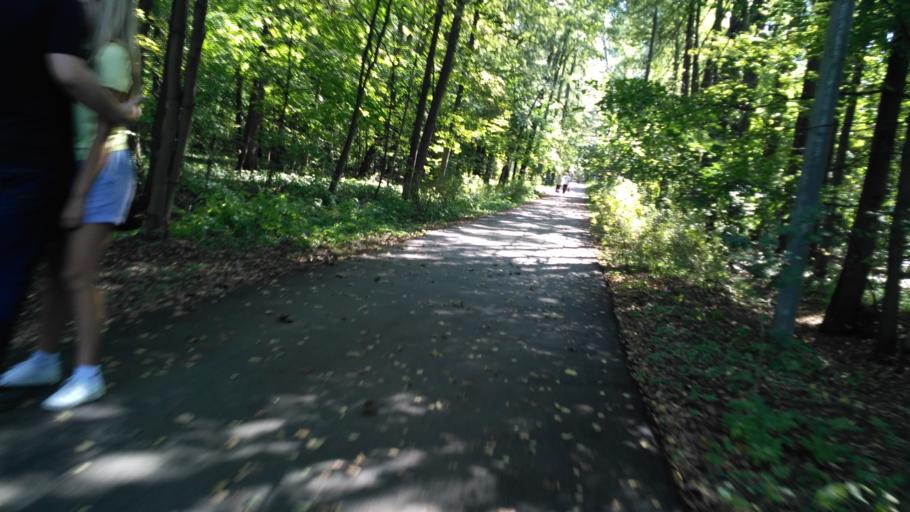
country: RU
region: Moscow
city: Metrogorodok
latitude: 55.7766
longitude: 37.7590
